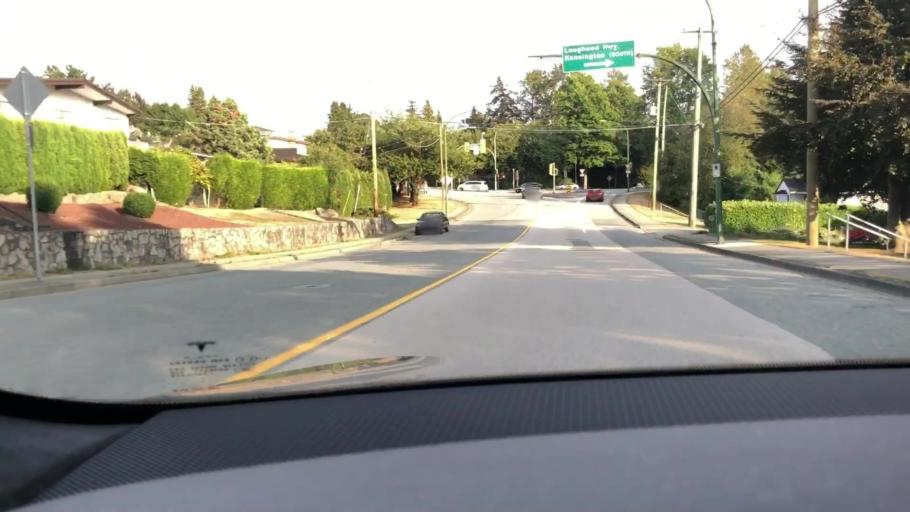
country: CA
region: British Columbia
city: Burnaby
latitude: 49.2624
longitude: -122.9697
